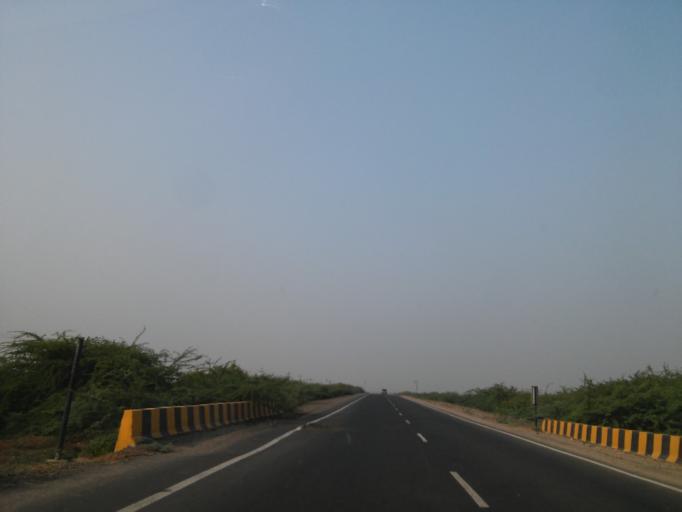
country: IN
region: Gujarat
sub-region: Kachchh
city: Anjar
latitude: 23.2950
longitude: 70.0543
